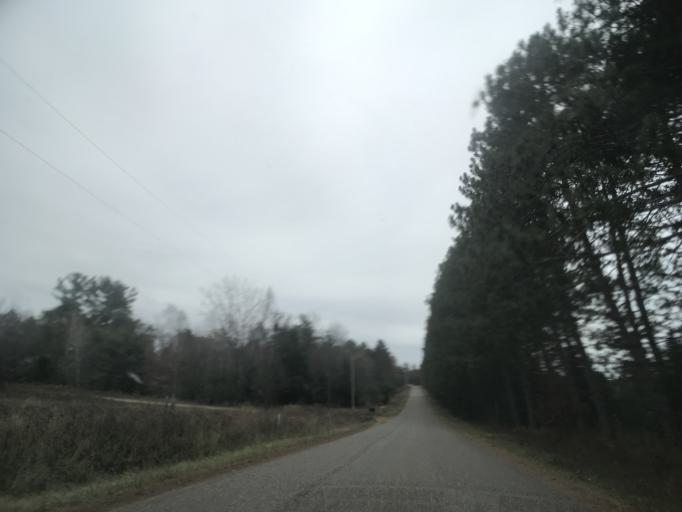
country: US
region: Michigan
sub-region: Dickinson County
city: Kingsford
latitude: 45.3886
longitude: -88.3226
